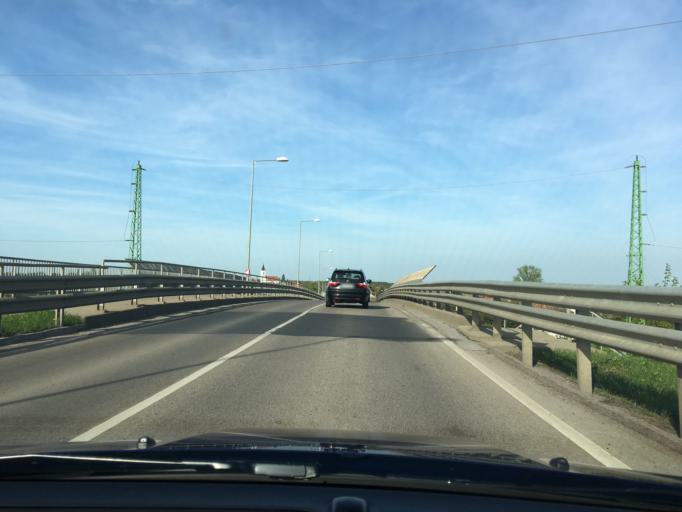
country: HU
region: Bekes
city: Mezobereny
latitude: 46.8118
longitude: 21.0143
